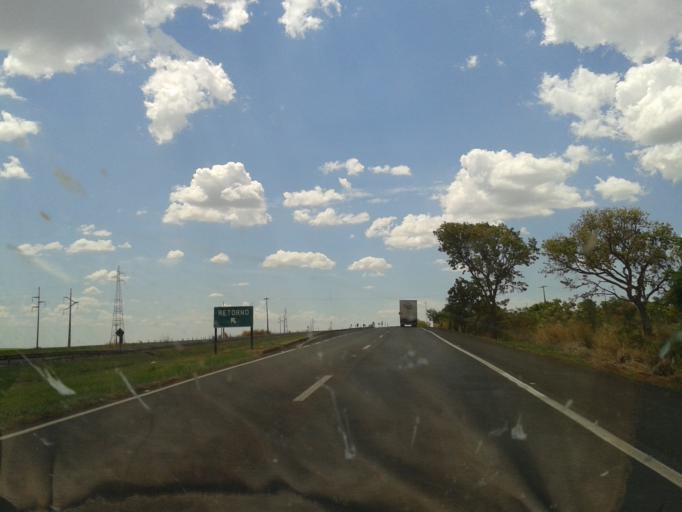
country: BR
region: Minas Gerais
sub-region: Uberlandia
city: Uberlandia
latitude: -19.0809
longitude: -48.1871
